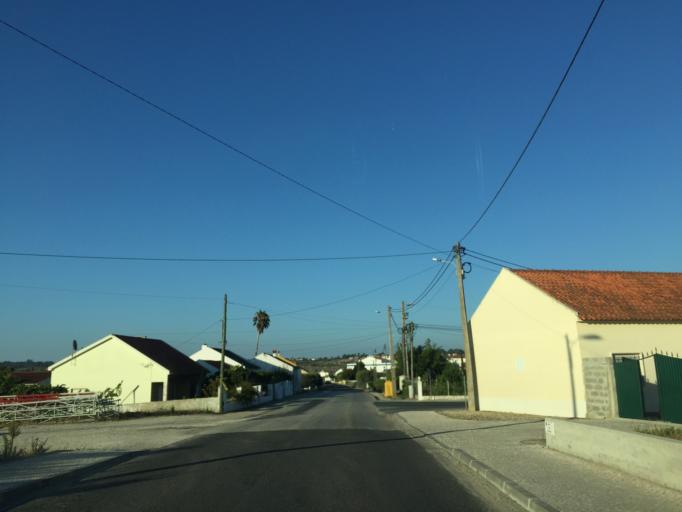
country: PT
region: Lisbon
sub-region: Azambuja
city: Aveiras de Cima
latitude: 39.1403
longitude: -8.9052
